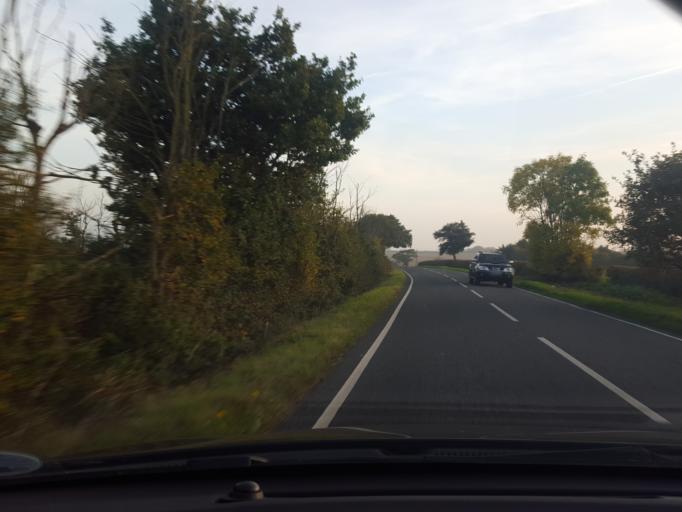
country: GB
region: England
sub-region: Essex
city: Little Clacton
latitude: 51.8347
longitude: 1.1555
